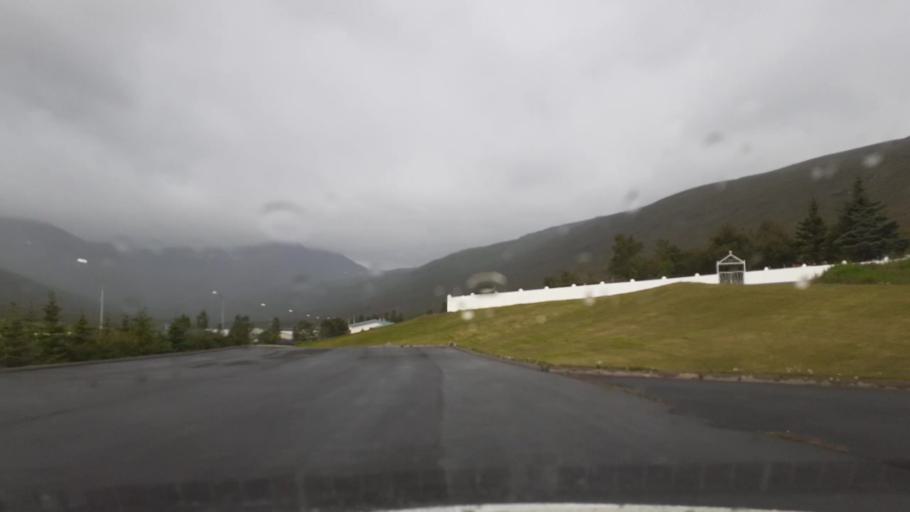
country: IS
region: East
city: Eskifjoerdur
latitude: 65.0787
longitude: -14.0349
